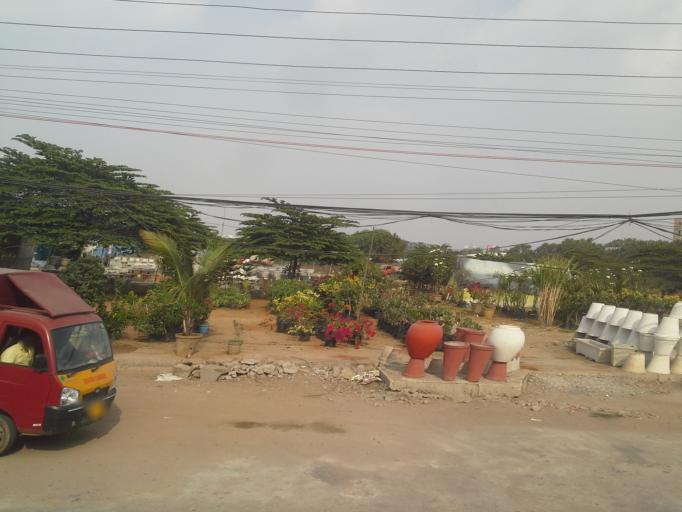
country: IN
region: Telangana
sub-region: Rangareddi
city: Kukatpalli
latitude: 17.4551
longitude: 78.3782
